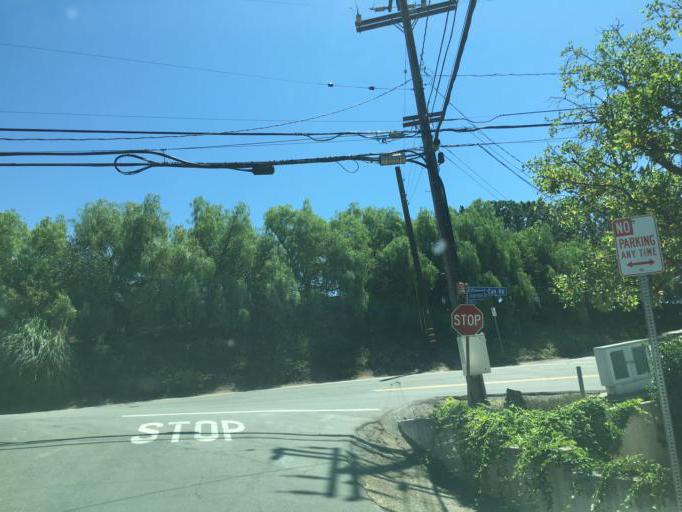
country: US
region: California
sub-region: Los Angeles County
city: Malibu Beach
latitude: 34.0436
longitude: -118.7396
